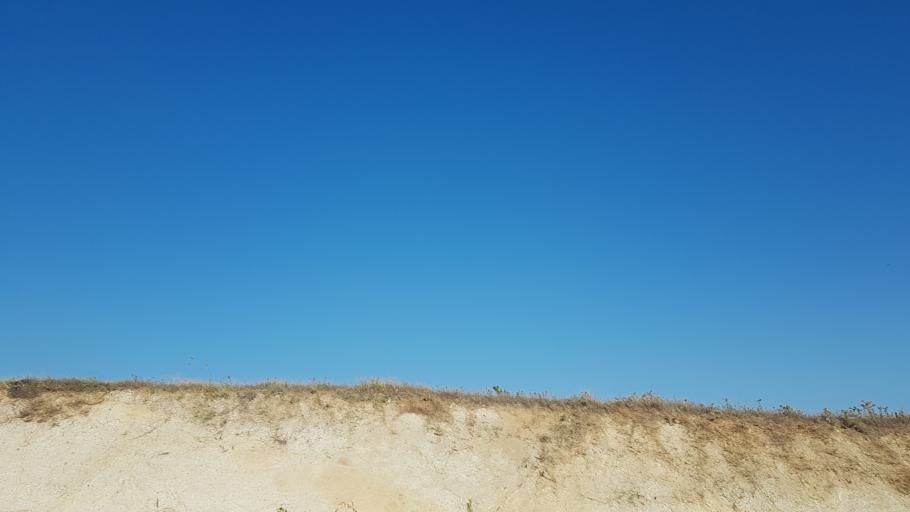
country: TR
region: Balikesir
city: Ertugrul
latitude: 39.6266
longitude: 27.7050
